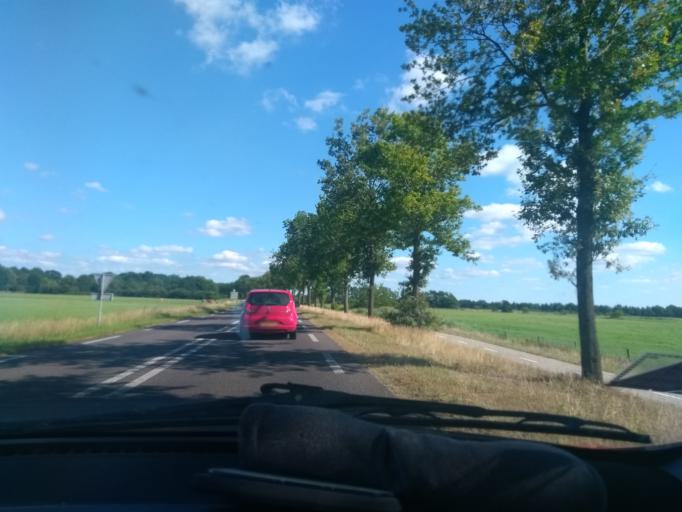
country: NL
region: Drenthe
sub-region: Gemeente Tynaarlo
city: Vries
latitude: 53.1105
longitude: 6.5192
